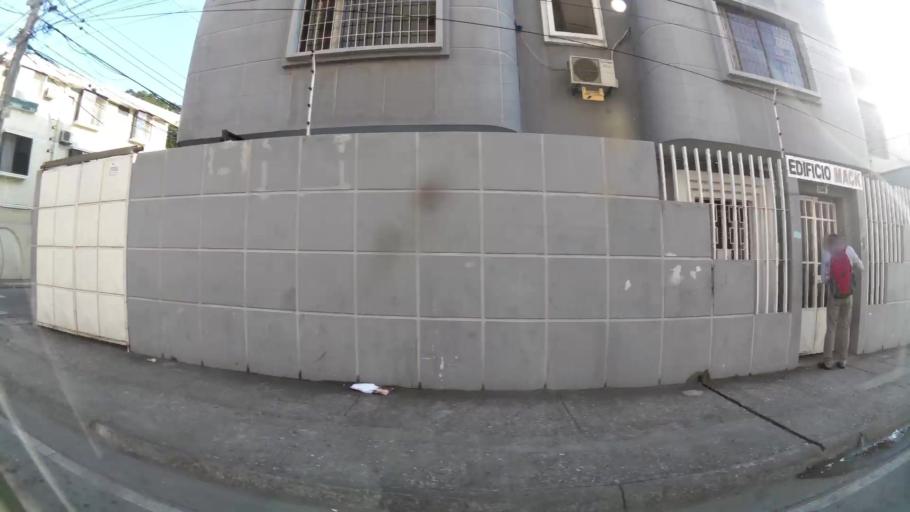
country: EC
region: Guayas
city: Eloy Alfaro
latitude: -2.1677
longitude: -79.8934
